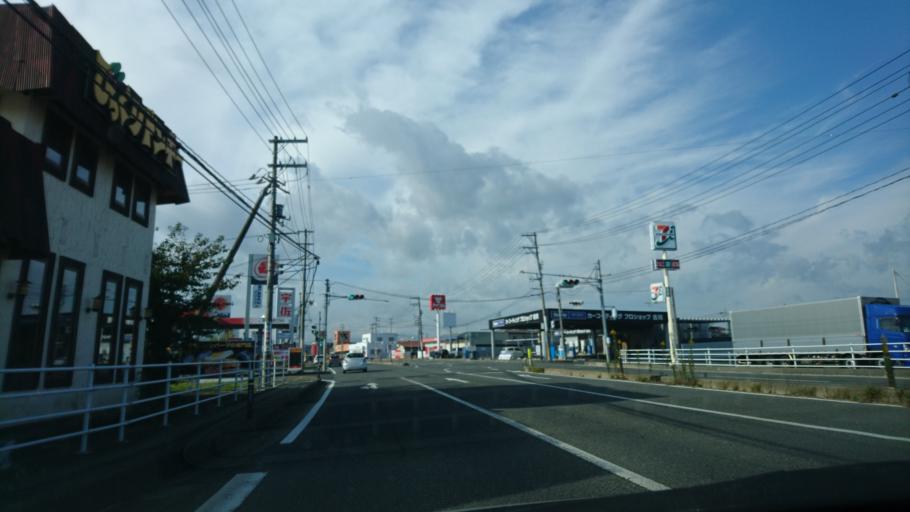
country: JP
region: Miyagi
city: Furukawa
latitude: 38.5890
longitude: 140.9541
